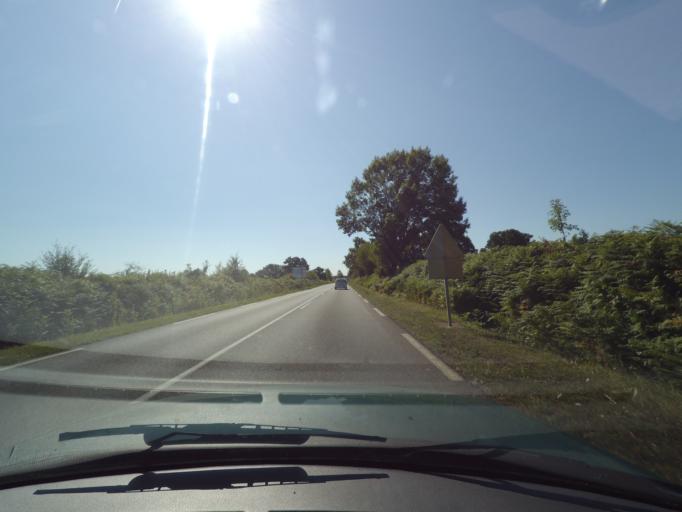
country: FR
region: Limousin
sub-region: Departement de la Haute-Vienne
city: Peyrat-de-Bellac
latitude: 46.1335
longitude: 0.9869
